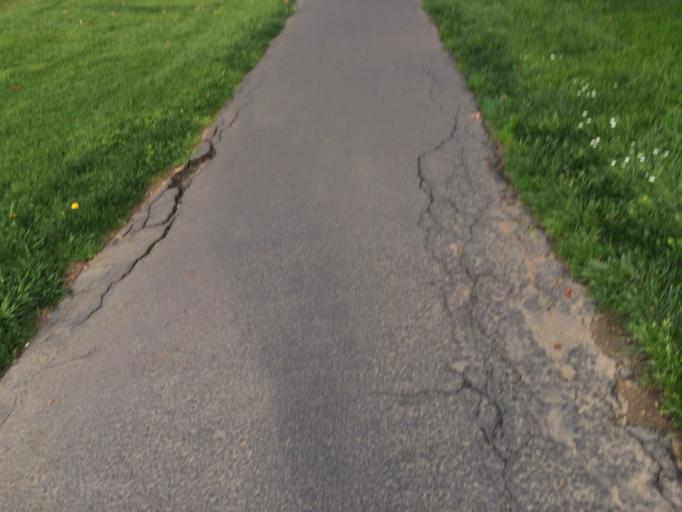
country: US
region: California
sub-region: Santa Clara County
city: Cupertino
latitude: 37.3186
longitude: -122.0198
